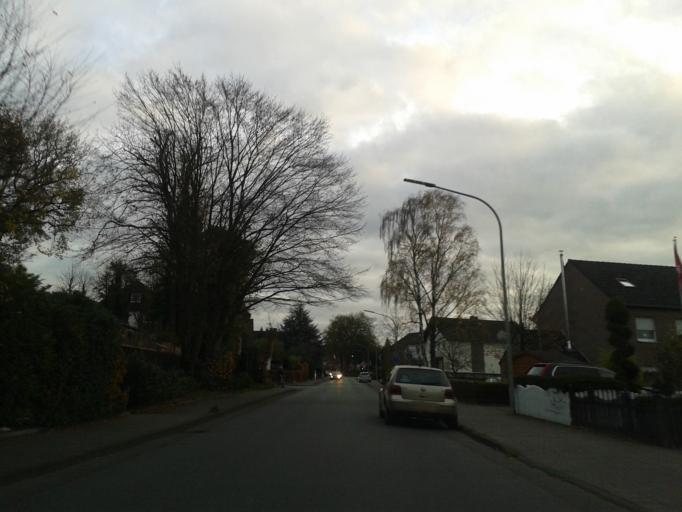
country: DE
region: North Rhine-Westphalia
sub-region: Regierungsbezirk Detmold
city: Paderborn
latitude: 51.7566
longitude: 8.7323
